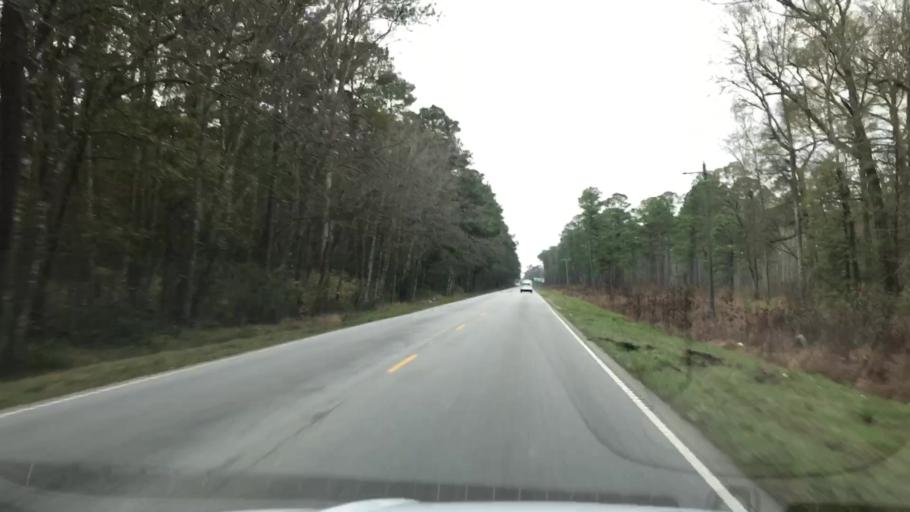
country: US
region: South Carolina
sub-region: Jasper County
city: Ridgeland
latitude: 32.3635
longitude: -80.9186
